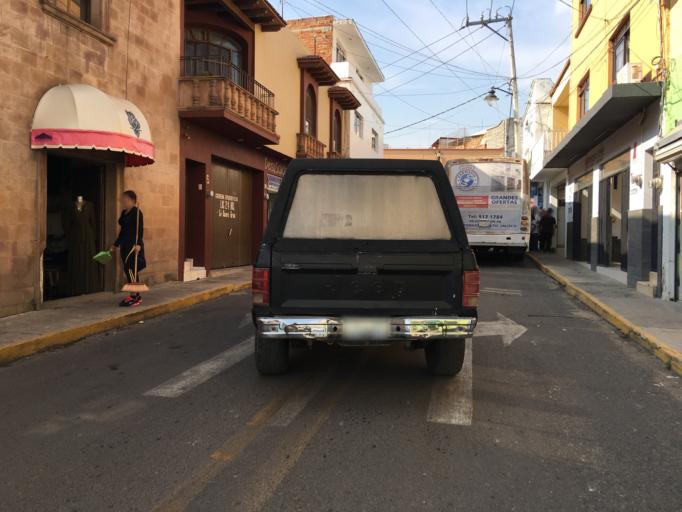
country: MX
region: Jalisco
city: Atotonilco el Alto
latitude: 20.5509
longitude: -102.5095
